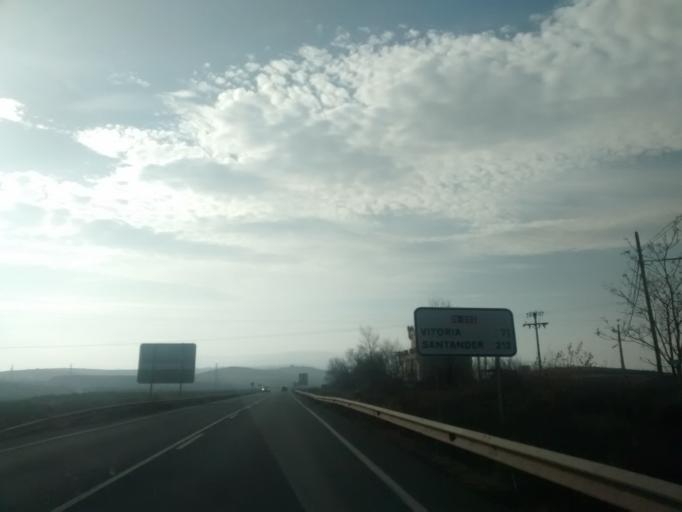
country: ES
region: La Rioja
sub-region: Provincia de La Rioja
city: Fuenmayor
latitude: 42.4611
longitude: -2.5744
